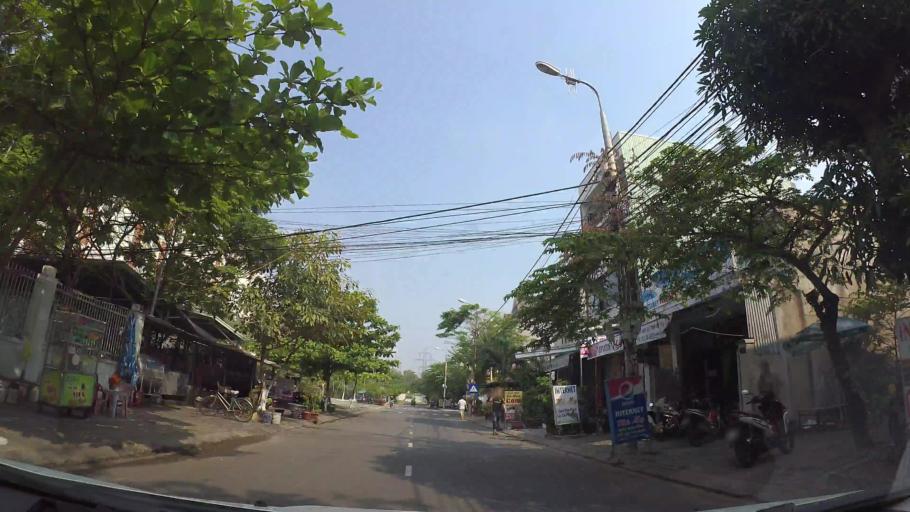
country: VN
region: Da Nang
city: Ngu Hanh Son
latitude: 16.0353
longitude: 108.2430
